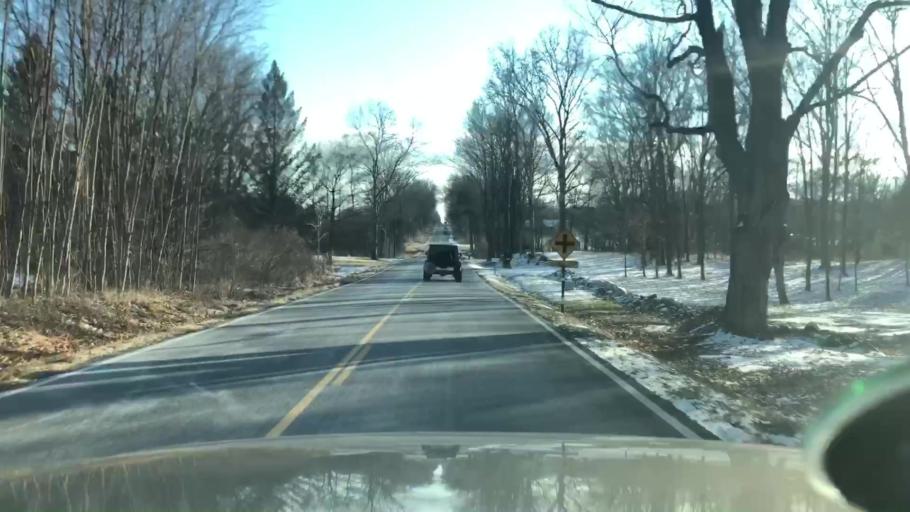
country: US
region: Michigan
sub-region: Jackson County
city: Vandercook Lake
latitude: 42.1322
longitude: -84.4516
